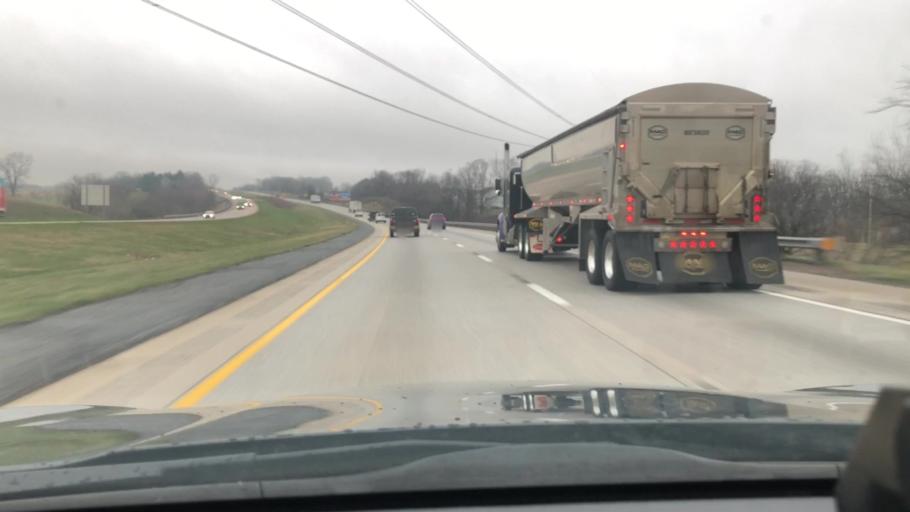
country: US
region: Pennsylvania
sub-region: Dauphin County
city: Skyline View
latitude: 40.3677
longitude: -76.6912
